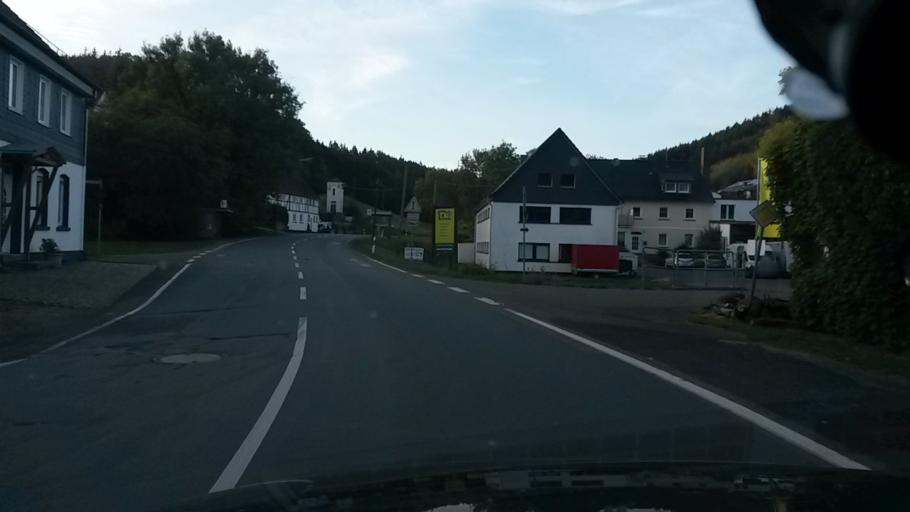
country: DE
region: North Rhine-Westphalia
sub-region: Regierungsbezirk Koln
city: Marienheide
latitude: 51.0595
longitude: 7.5164
